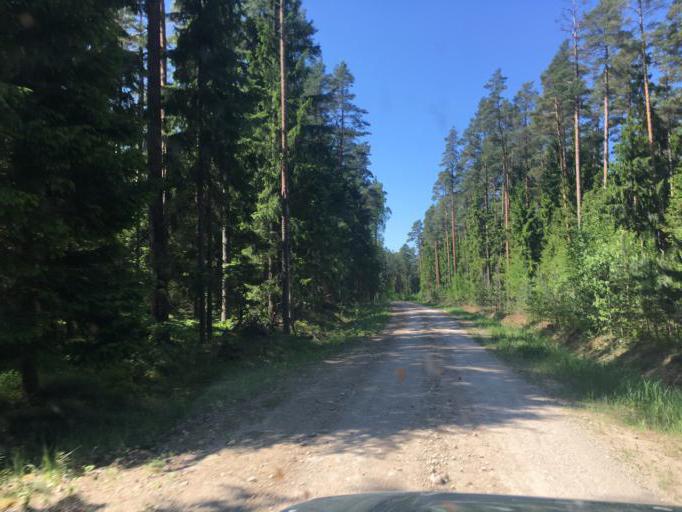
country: LV
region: Talsu Rajons
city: Valdemarpils
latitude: 57.4403
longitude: 22.6718
